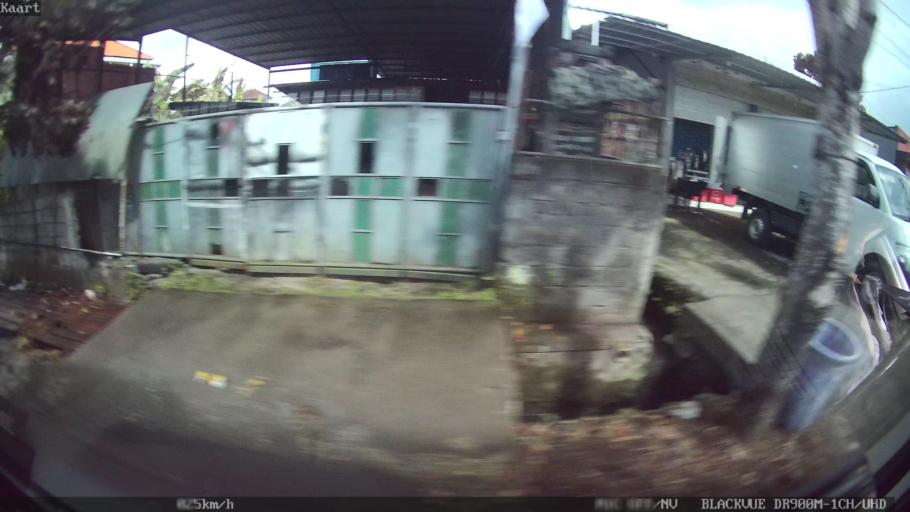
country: ID
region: Bali
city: Banjar Batur
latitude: -8.6040
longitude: 115.2061
